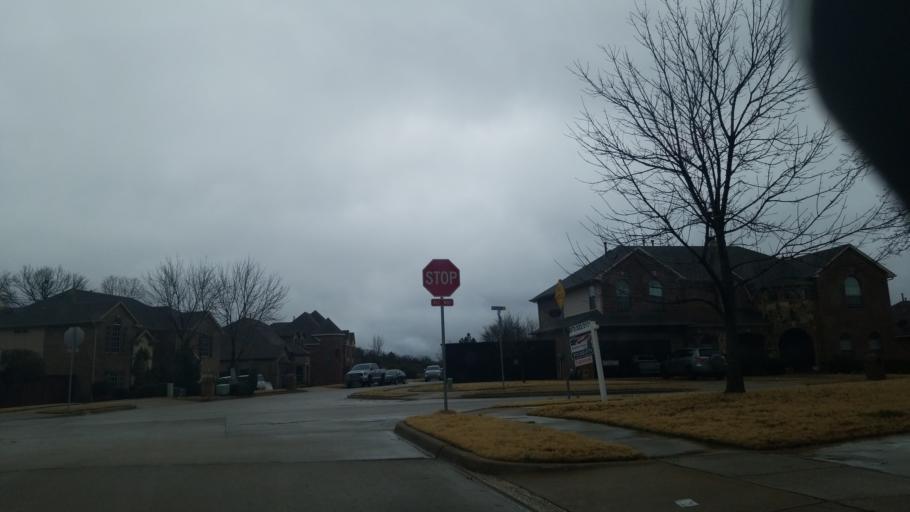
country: US
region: Texas
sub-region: Denton County
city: Corinth
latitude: 33.1369
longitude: -97.0913
